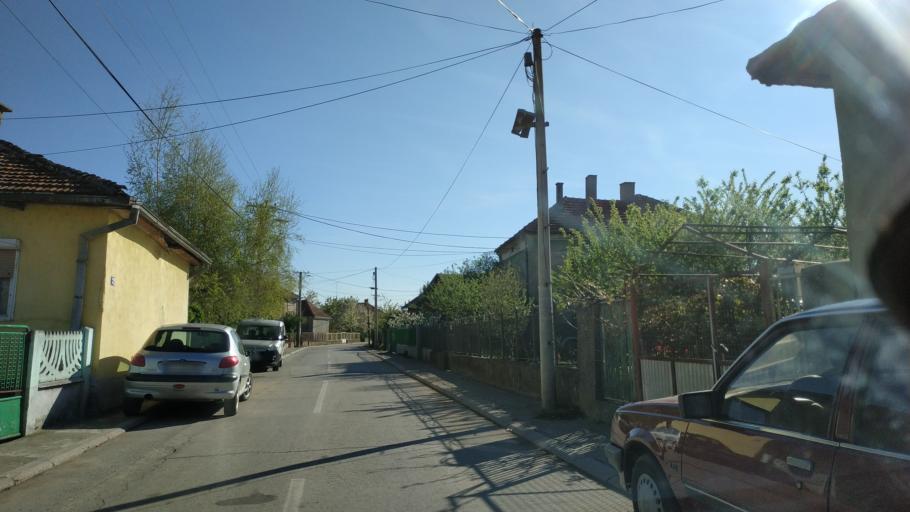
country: RS
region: Central Serbia
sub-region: Nisavski Okrug
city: Aleksinac
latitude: 43.5456
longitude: 21.7126
